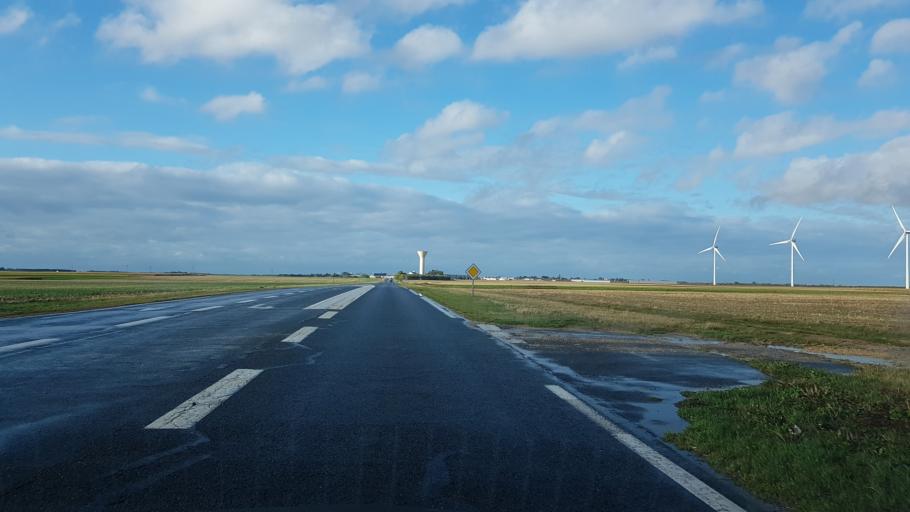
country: FR
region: Centre
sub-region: Departement du Loiret
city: Sermaises
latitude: 48.2703
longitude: 2.2110
